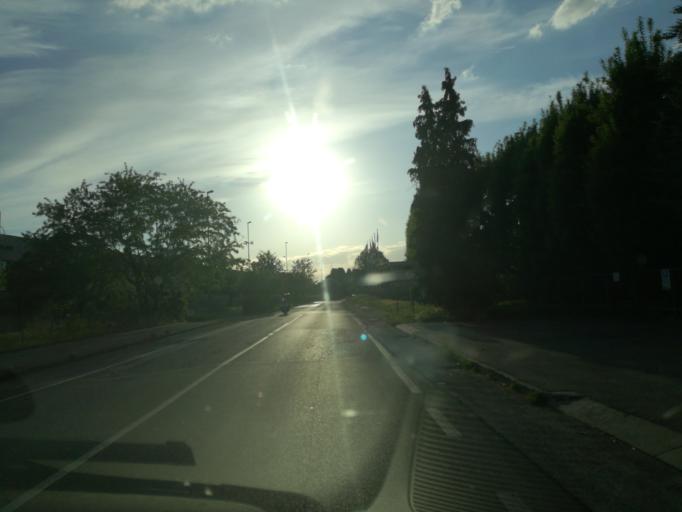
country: IT
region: Lombardy
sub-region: Provincia di Monza e Brianza
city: Ronco Briantino
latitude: 45.6774
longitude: 9.4078
